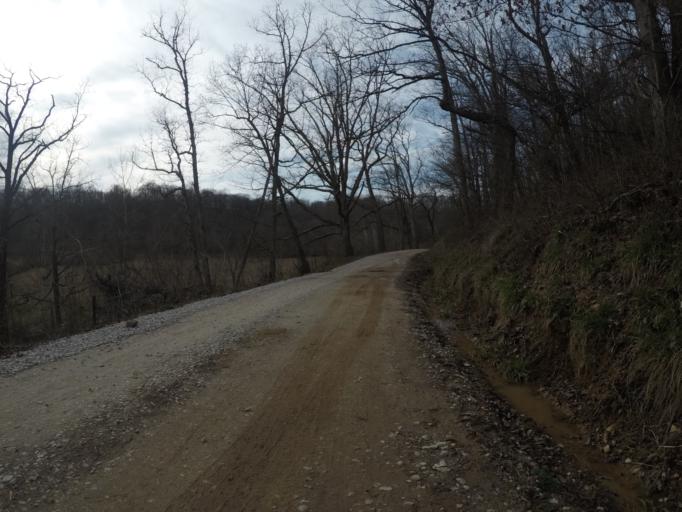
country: US
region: Ohio
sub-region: Lawrence County
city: Burlington
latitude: 38.4621
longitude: -82.5359
